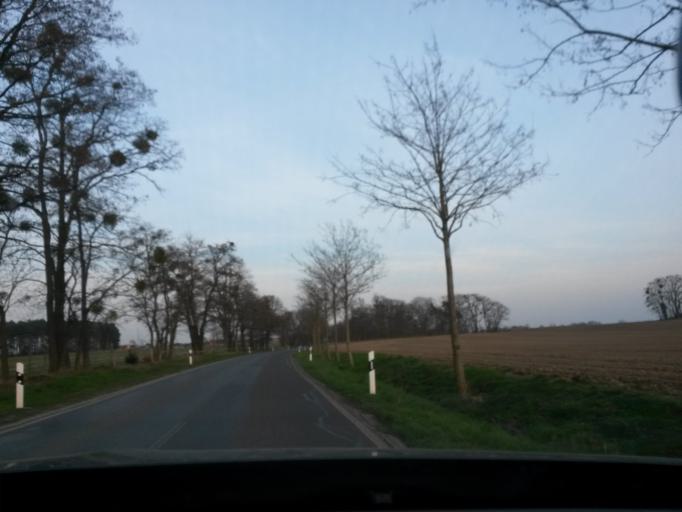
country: DE
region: Brandenburg
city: Strausberg
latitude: 52.5962
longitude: 13.9388
